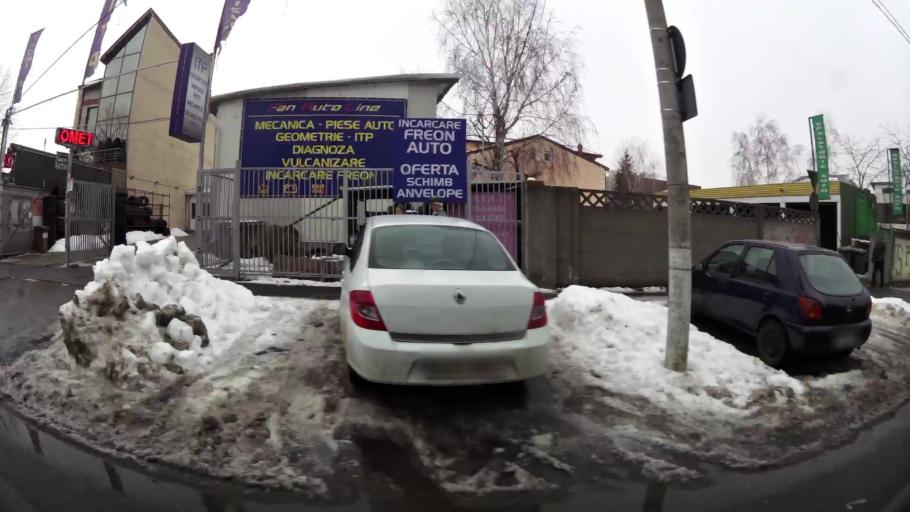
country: RO
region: Ilfov
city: Dobroesti
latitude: 44.4174
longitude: 26.1724
